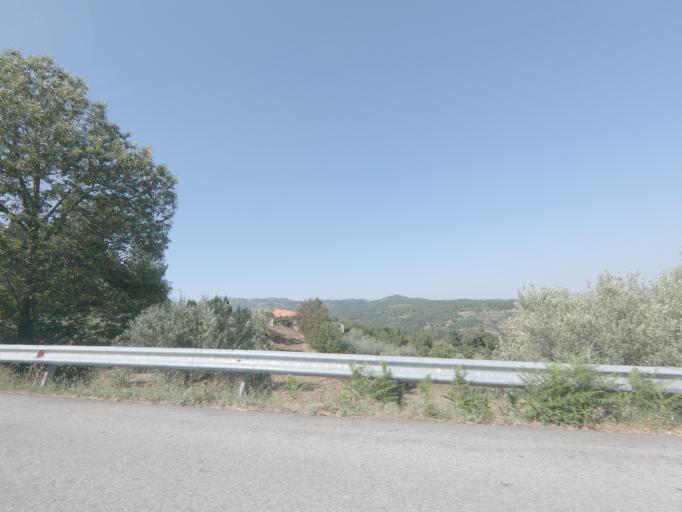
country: PT
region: Viseu
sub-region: Moimenta da Beira
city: Moimenta da Beira
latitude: 40.9794
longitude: -7.5992
